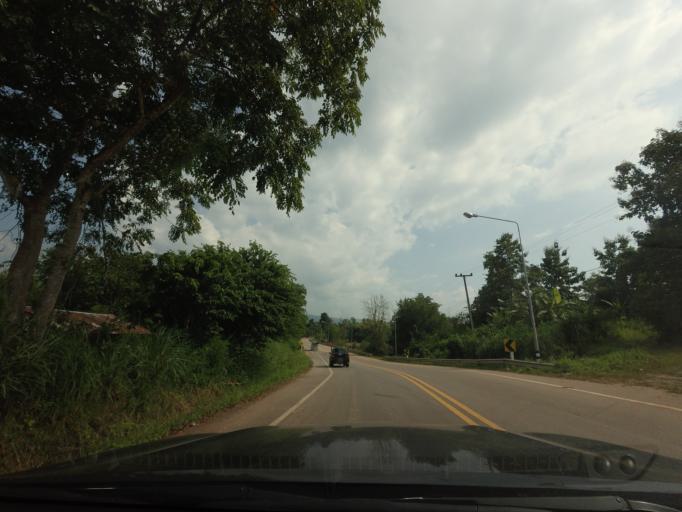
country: TH
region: Phitsanulok
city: Nakhon Thai
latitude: 17.0378
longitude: 100.9126
